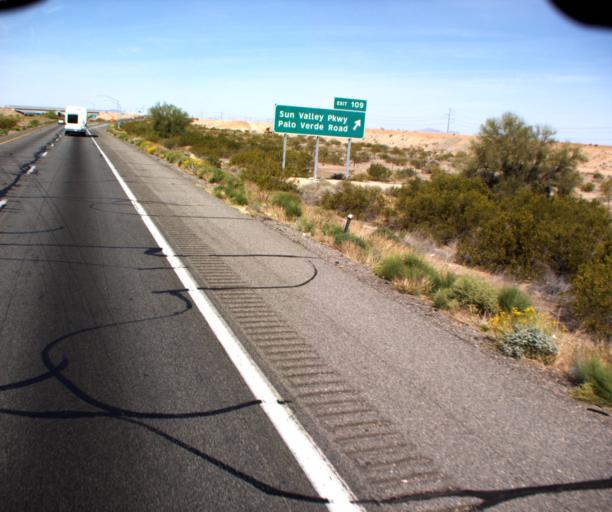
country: US
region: Arizona
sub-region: Maricopa County
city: Buckeye
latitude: 33.4379
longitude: -112.6705
